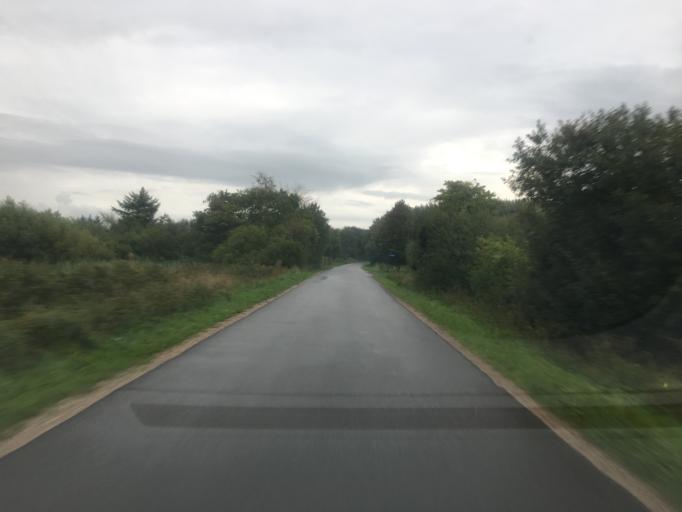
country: DK
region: South Denmark
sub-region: Tonder Kommune
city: Logumkloster
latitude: 54.9910
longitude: 8.9776
